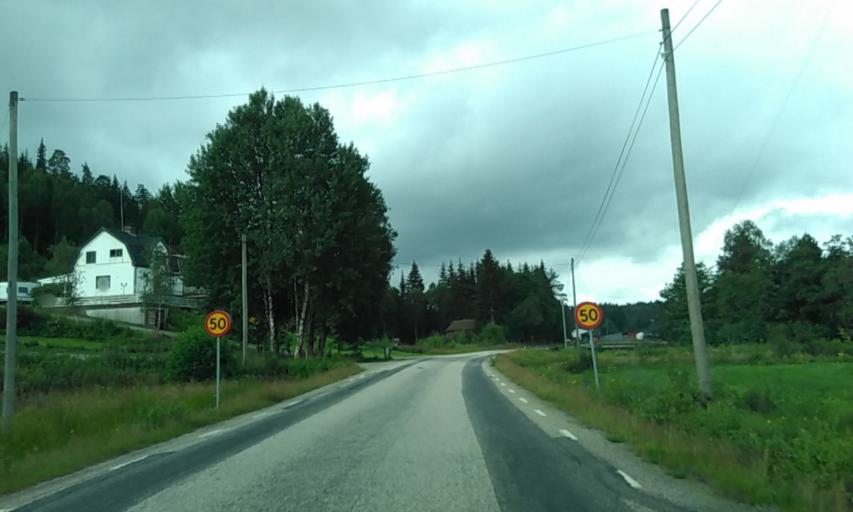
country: SE
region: Vaestra Goetaland
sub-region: Bollebygds Kommun
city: Bollebygd
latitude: 57.7362
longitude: 12.5942
